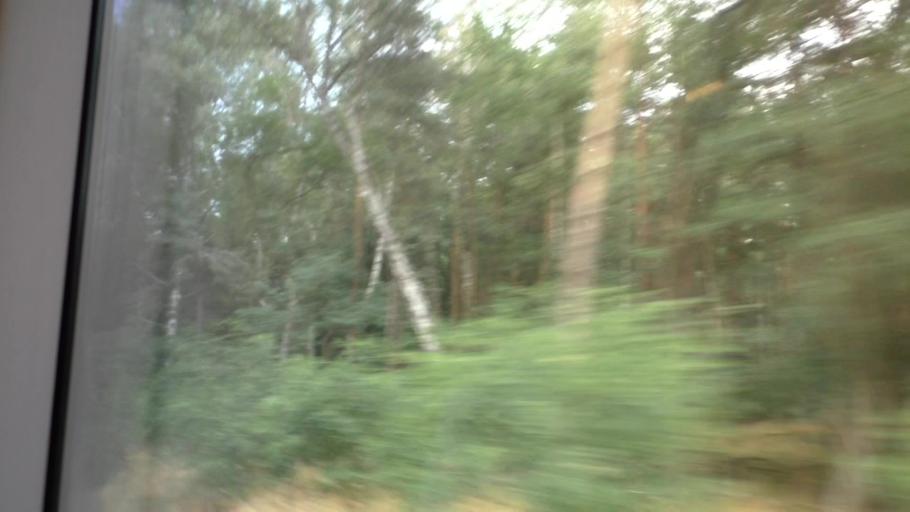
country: DE
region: Brandenburg
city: Mullrose
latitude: 52.2207
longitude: 14.4266
